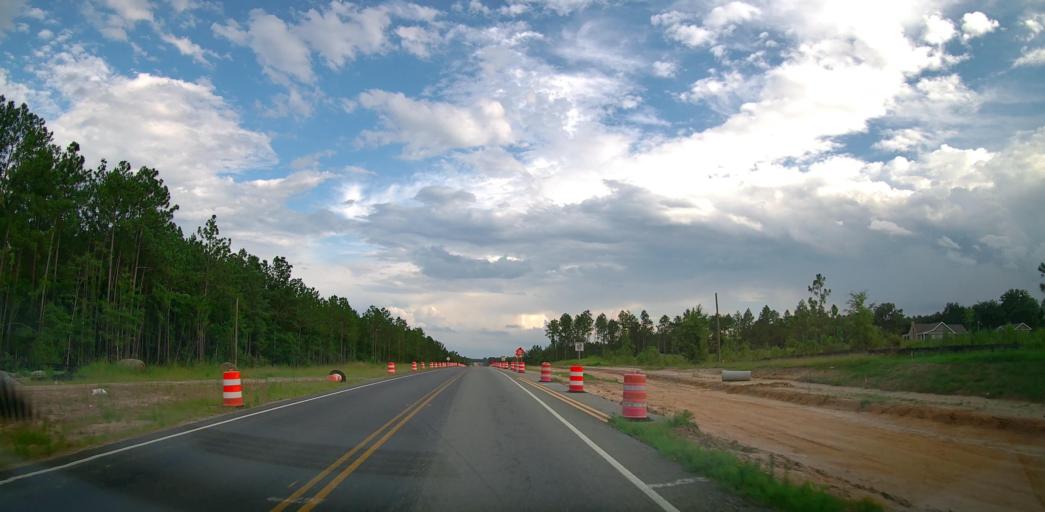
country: US
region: Georgia
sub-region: Dodge County
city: Eastman
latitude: 32.2710
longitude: -83.2466
